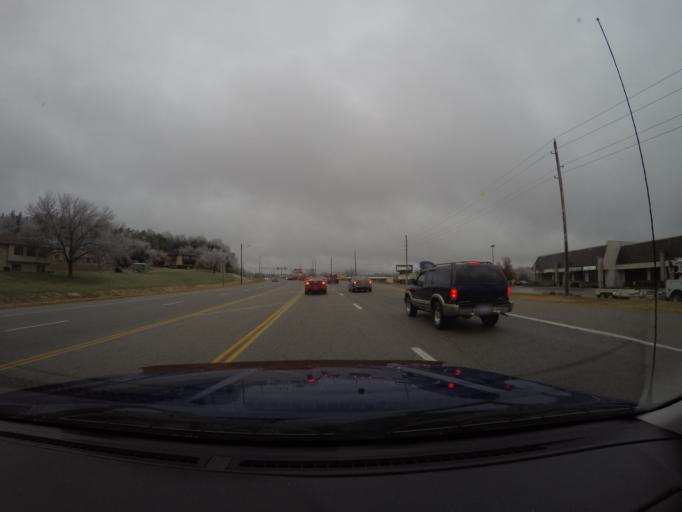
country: US
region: Kansas
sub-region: Riley County
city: Manhattan
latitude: 39.1751
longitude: -96.6039
